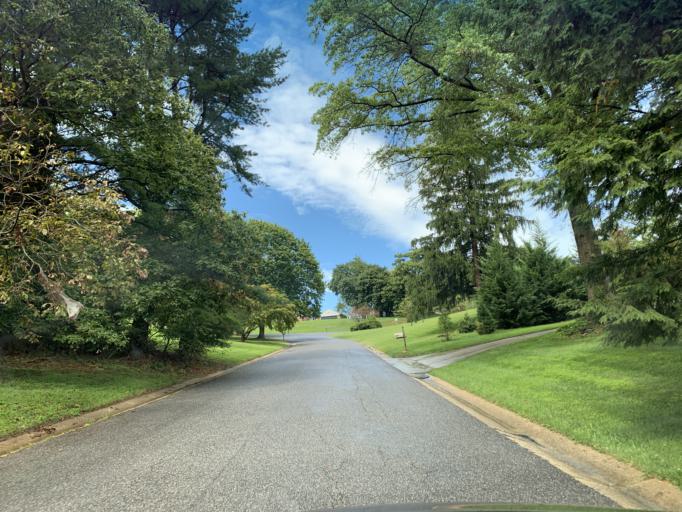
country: US
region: Maryland
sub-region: Baltimore County
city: Timonium
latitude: 39.4457
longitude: -76.6228
